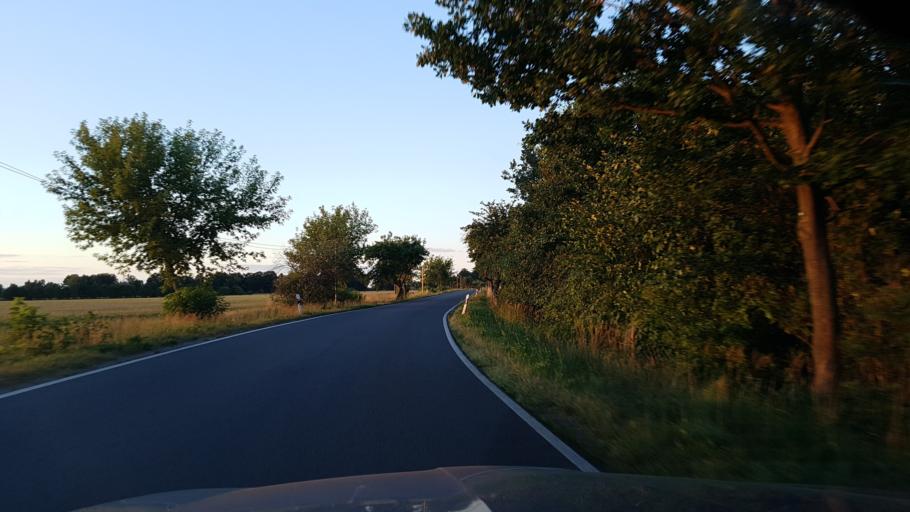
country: DE
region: Brandenburg
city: Groden
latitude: 51.4122
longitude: 13.5903
